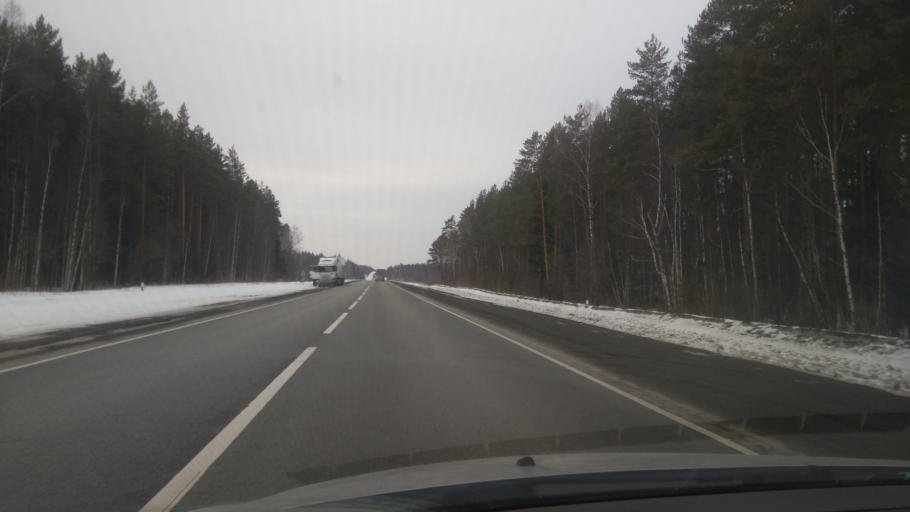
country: RU
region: Sverdlovsk
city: Bisert'
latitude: 56.8280
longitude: 58.7731
